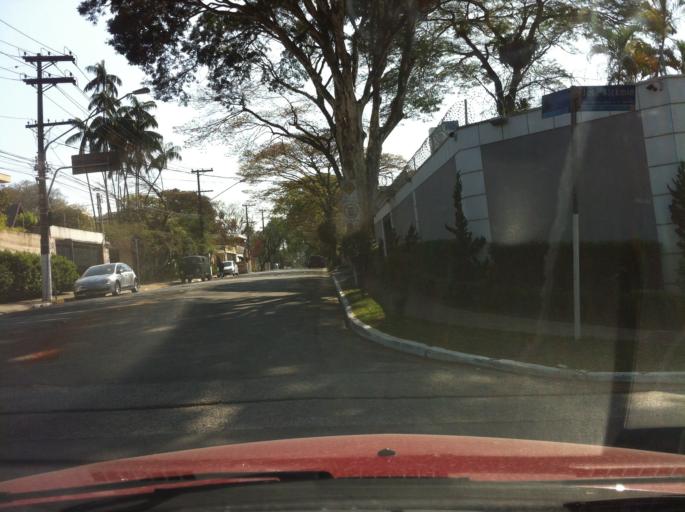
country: BR
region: Sao Paulo
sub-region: Diadema
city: Diadema
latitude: -23.6365
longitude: -46.6899
